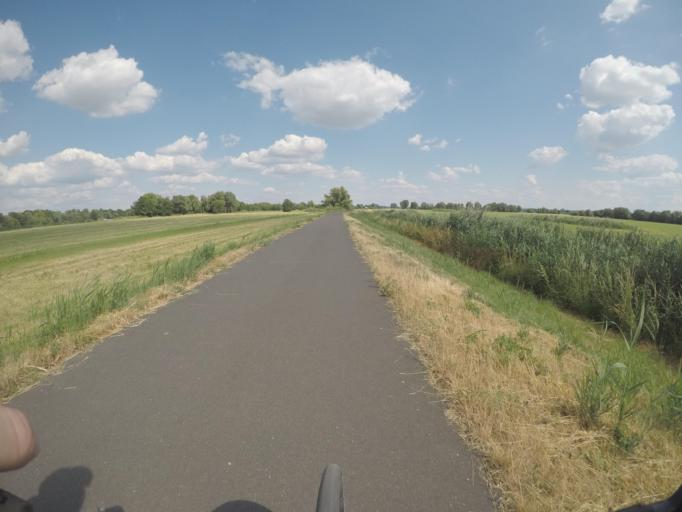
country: DE
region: Brandenburg
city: Ketzin
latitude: 52.4681
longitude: 12.8346
